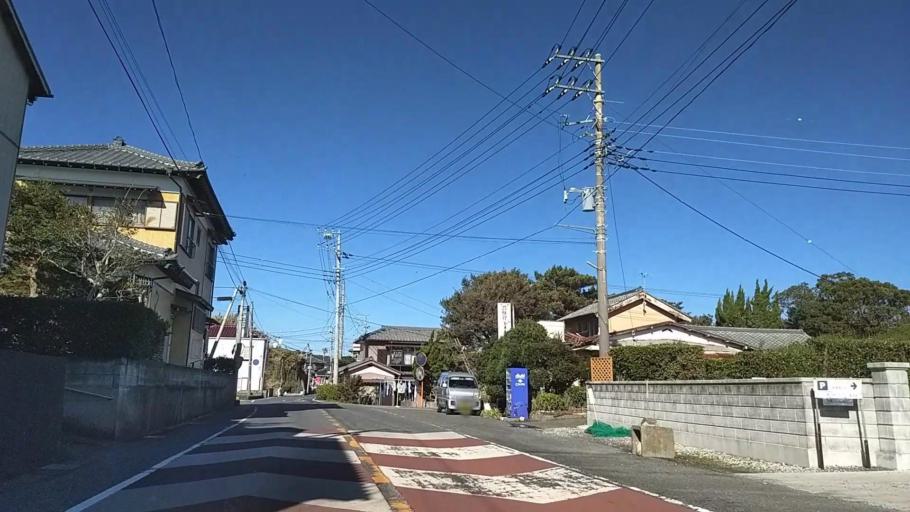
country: JP
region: Chiba
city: Tateyama
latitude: 34.9485
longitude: 139.9630
